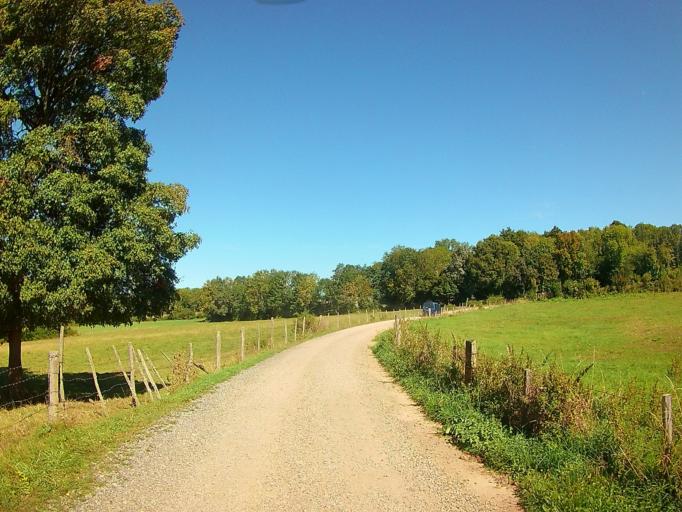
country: FR
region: Auvergne
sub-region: Departement du Puy-de-Dome
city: Chapdes-Beaufort
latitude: 45.8939
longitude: 2.8839
